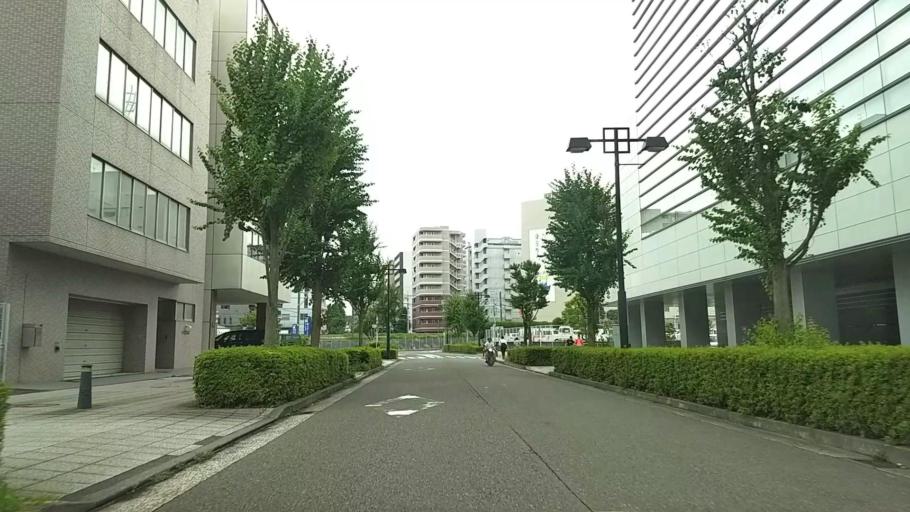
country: JP
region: Kanagawa
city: Yokohama
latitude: 35.5069
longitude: 139.6116
